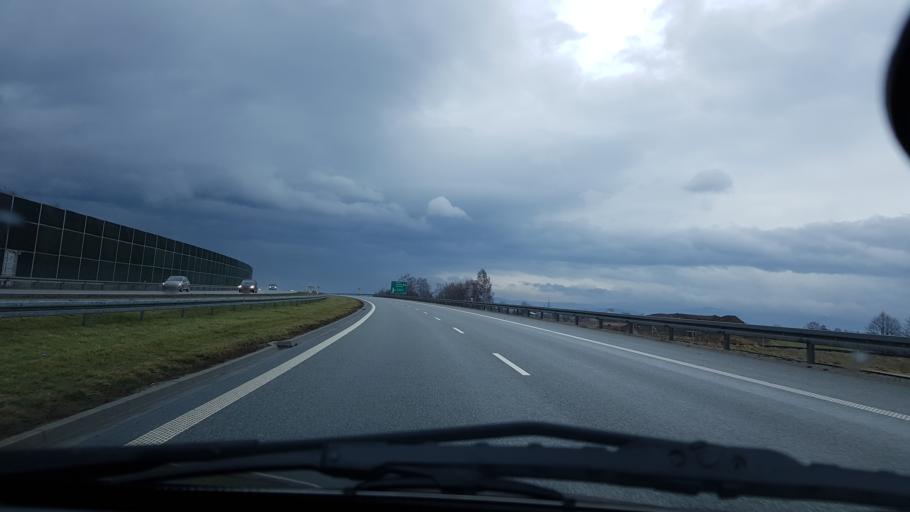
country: PL
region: Silesian Voivodeship
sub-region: Powiat bielski
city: Rybarzowice
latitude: 49.7430
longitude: 19.0938
